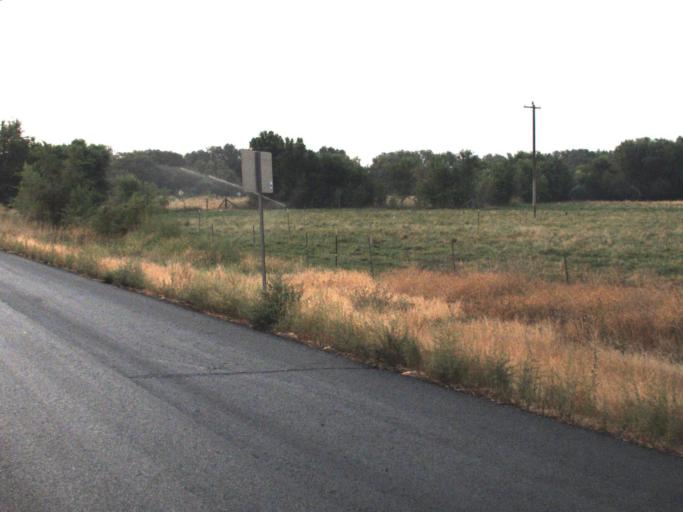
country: US
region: Washington
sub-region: Yakima County
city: Wapato
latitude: 46.4026
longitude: -120.3767
